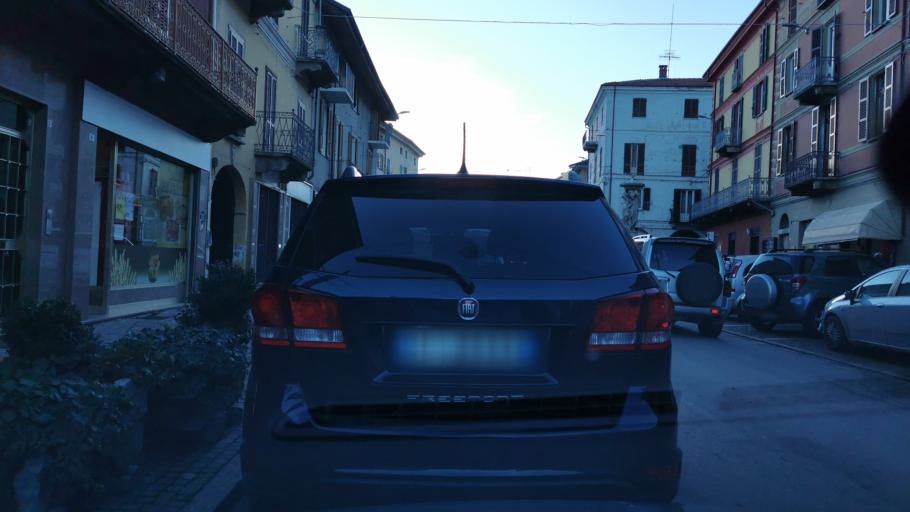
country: IT
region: Piedmont
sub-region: Provincia di Cuneo
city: Caraglio
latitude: 44.4177
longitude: 7.4285
